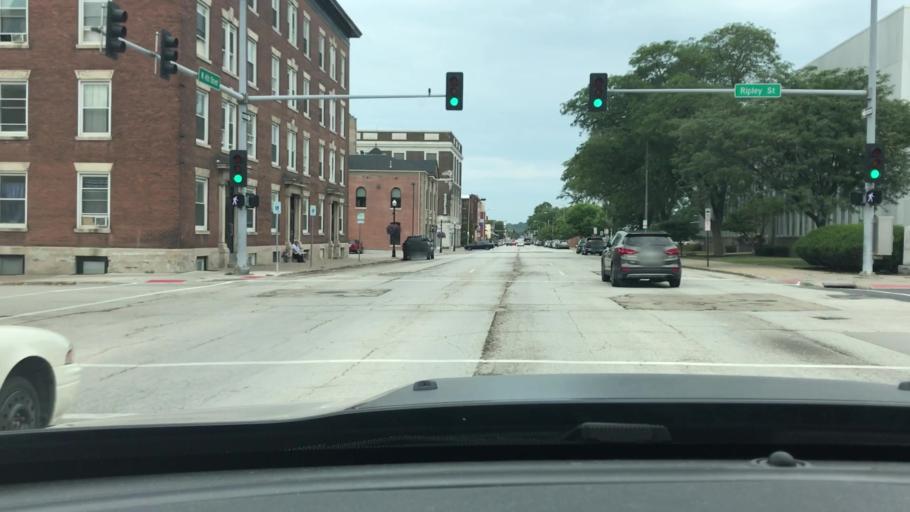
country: US
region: Iowa
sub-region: Scott County
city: Davenport
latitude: 41.5235
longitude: -90.5784
